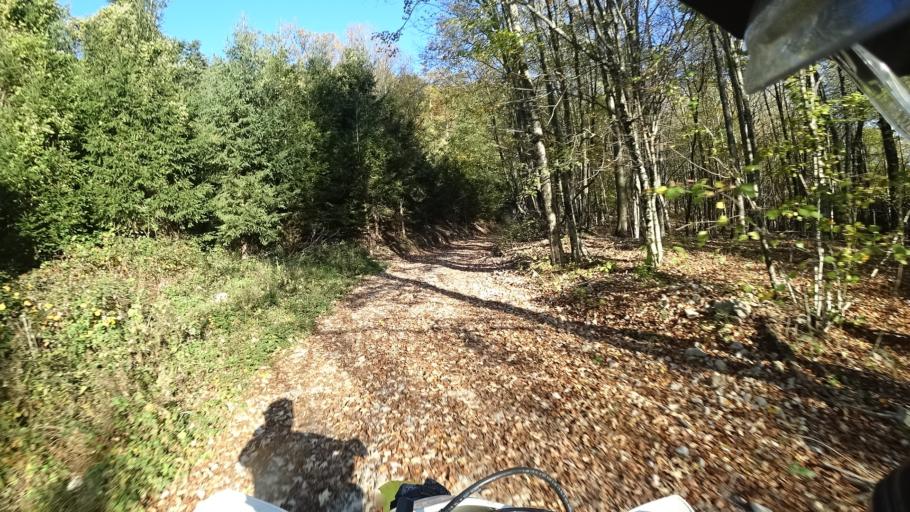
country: HR
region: Primorsko-Goranska
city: Klana
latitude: 45.4897
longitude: 14.4087
